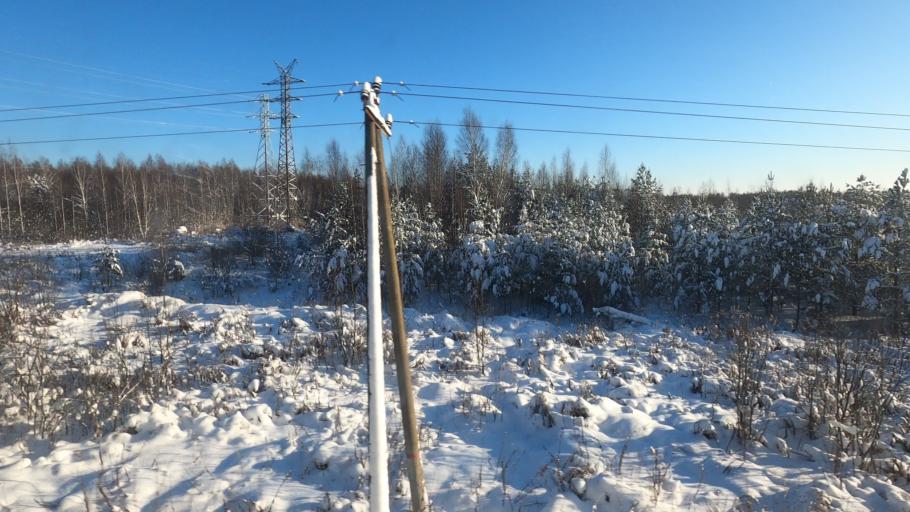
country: RU
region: Moskovskaya
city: Zhukovka
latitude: 56.4676
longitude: 37.5265
